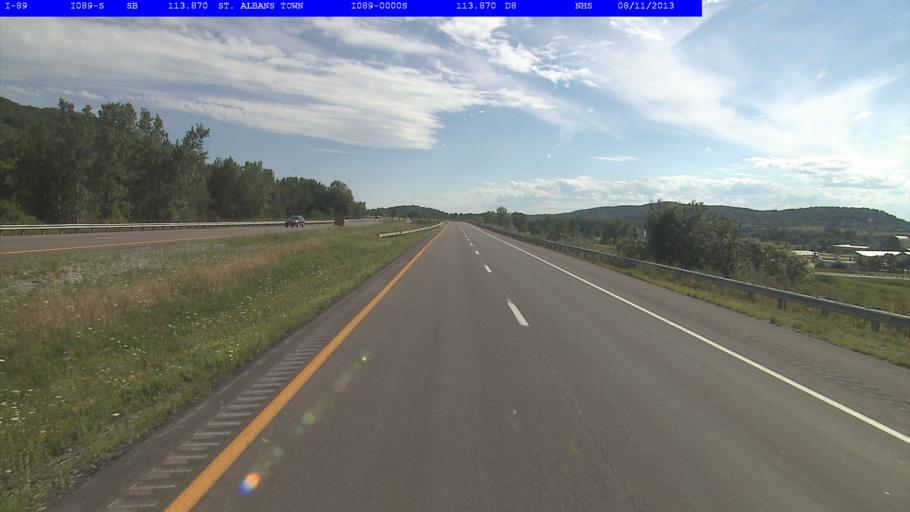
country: US
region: Vermont
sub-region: Franklin County
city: Saint Albans
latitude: 44.7966
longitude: -73.0687
